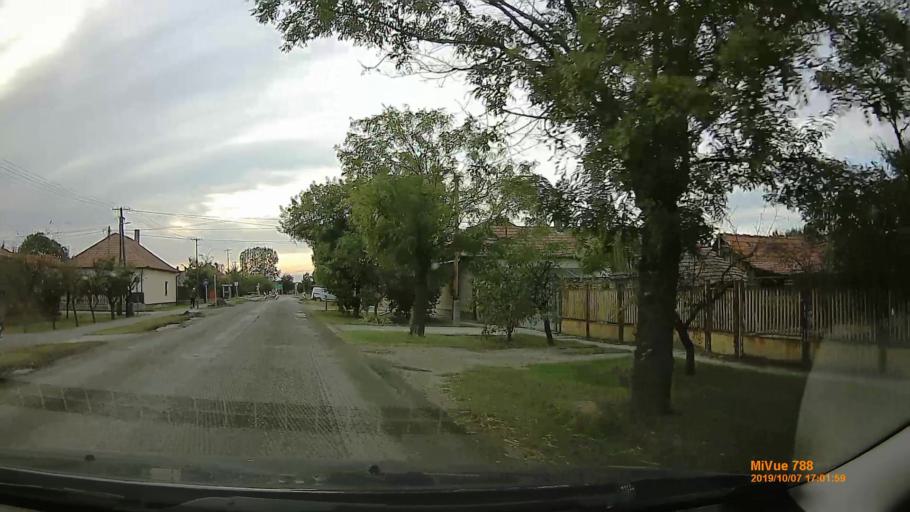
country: HU
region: Bekes
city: Szarvas
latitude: 46.8516
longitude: 20.5596
